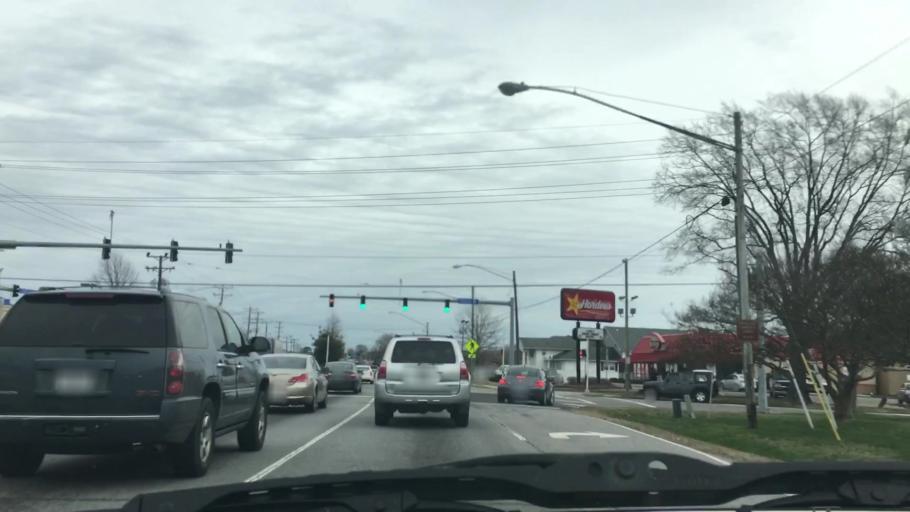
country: US
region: Virginia
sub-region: City of Norfolk
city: Norfolk
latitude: 36.9151
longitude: -76.2212
